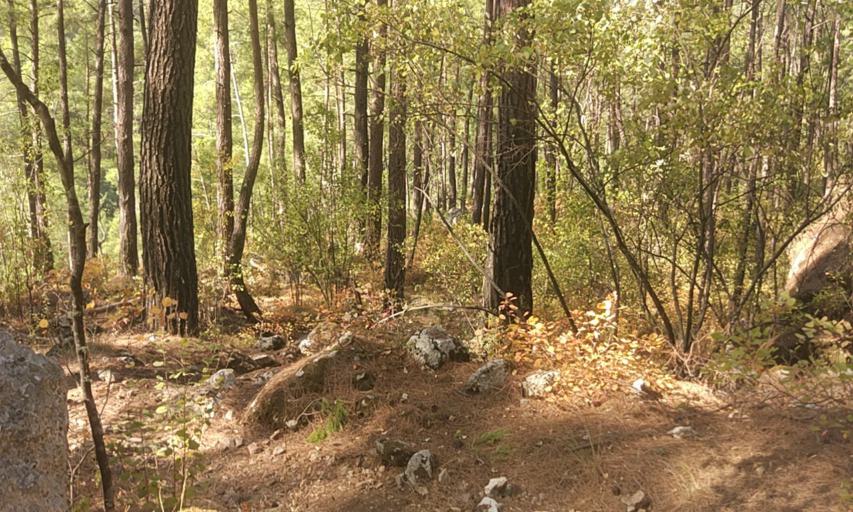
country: TR
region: Antalya
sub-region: Kemer
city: Goeynuek
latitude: 36.6750
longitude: 30.4977
